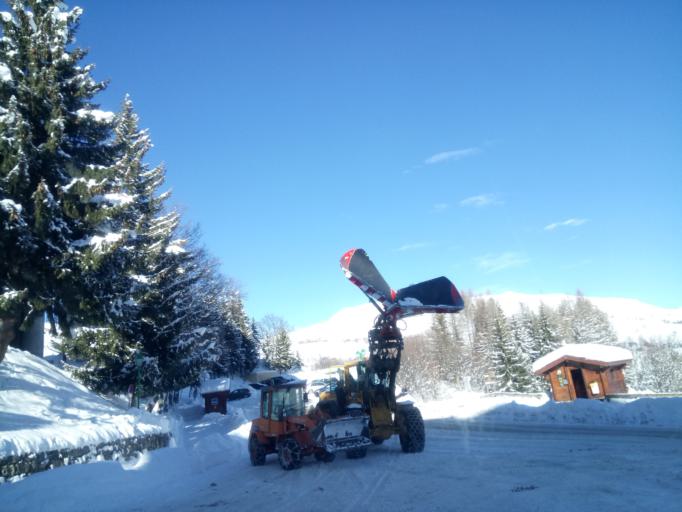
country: FR
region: Rhone-Alpes
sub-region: Departement de la Savoie
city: Saint-Jean-de-Maurienne
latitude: 45.2409
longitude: 6.2682
